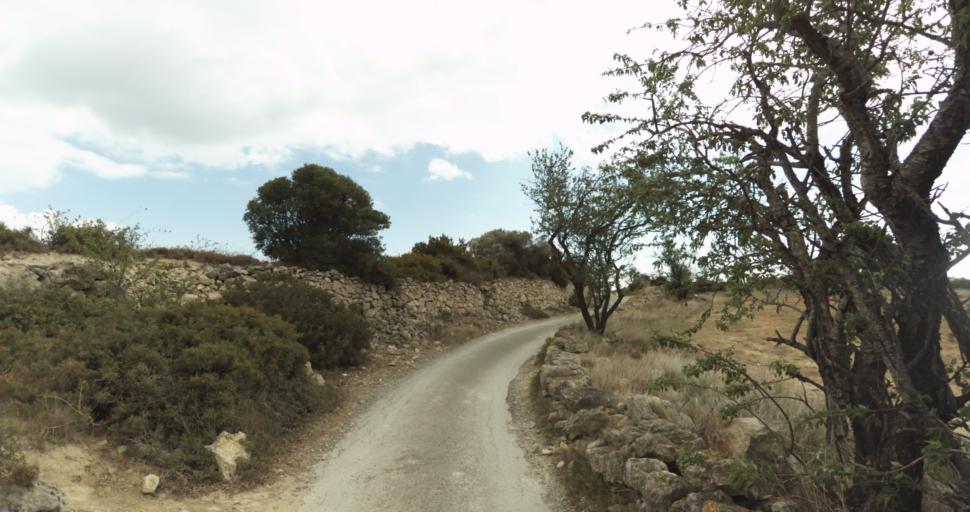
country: FR
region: Languedoc-Roussillon
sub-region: Departement de l'Aude
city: Leucate
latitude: 42.9127
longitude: 3.0388
